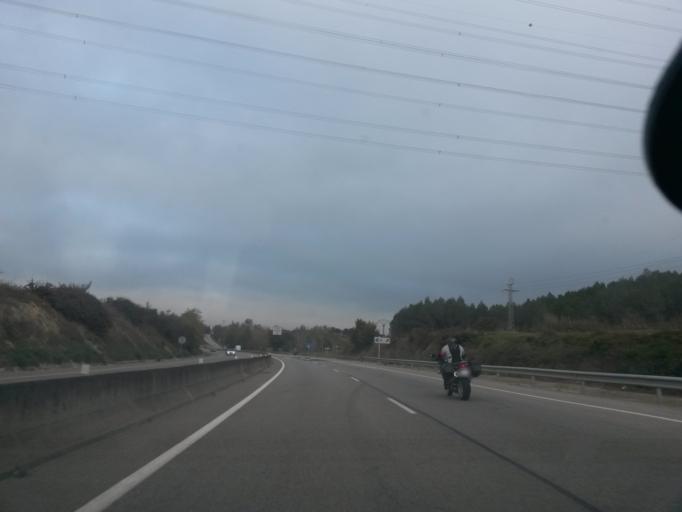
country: ES
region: Catalonia
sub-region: Provincia de Girona
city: Palol de Revardit
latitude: 42.0531
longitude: 2.8180
